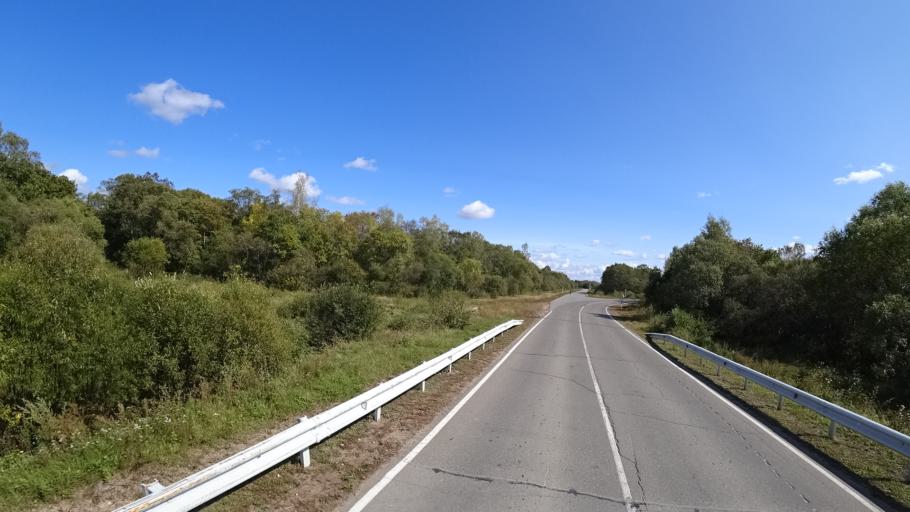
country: RU
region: Amur
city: Arkhara
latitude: 49.4061
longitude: 130.1245
